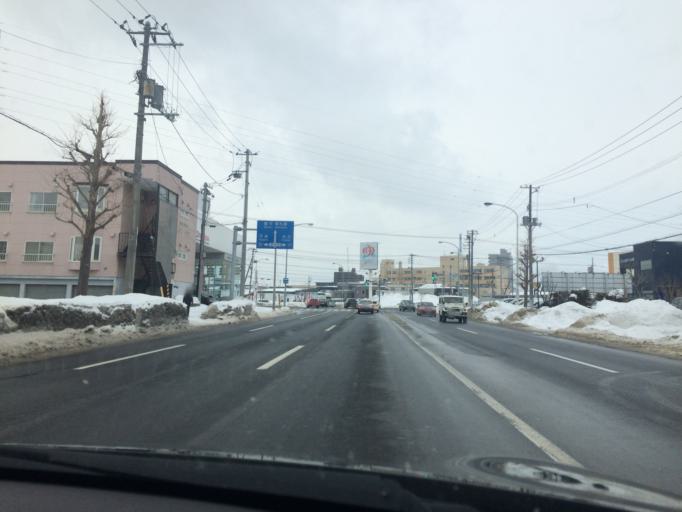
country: JP
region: Hokkaido
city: Sapporo
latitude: 43.0670
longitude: 141.4096
